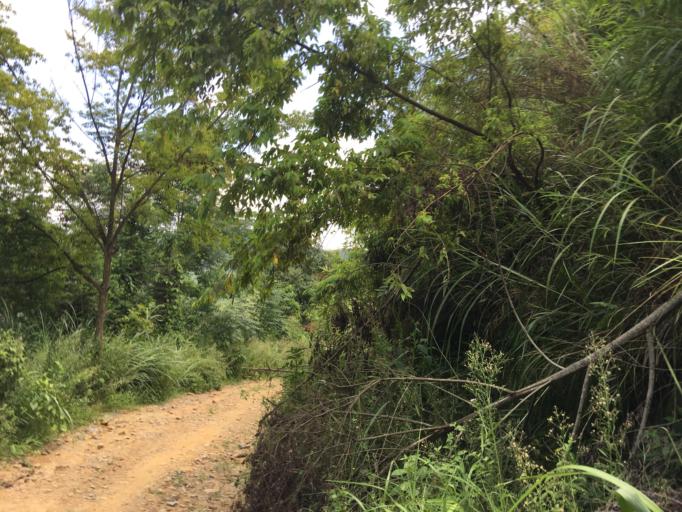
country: CN
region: Guangxi Zhuangzu Zizhiqu
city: Tongle
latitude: 24.9708
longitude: 105.9767
